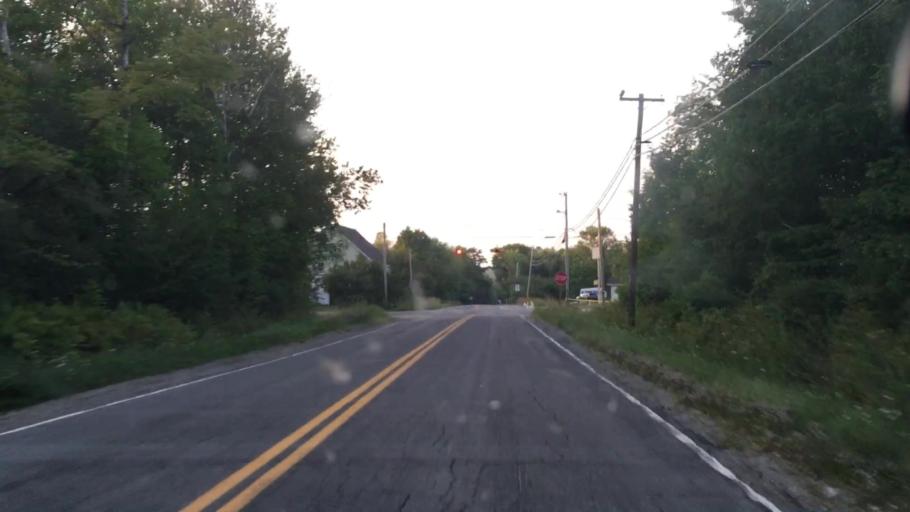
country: US
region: Maine
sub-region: Waldo County
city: Frankfort
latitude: 44.6978
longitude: -68.9441
